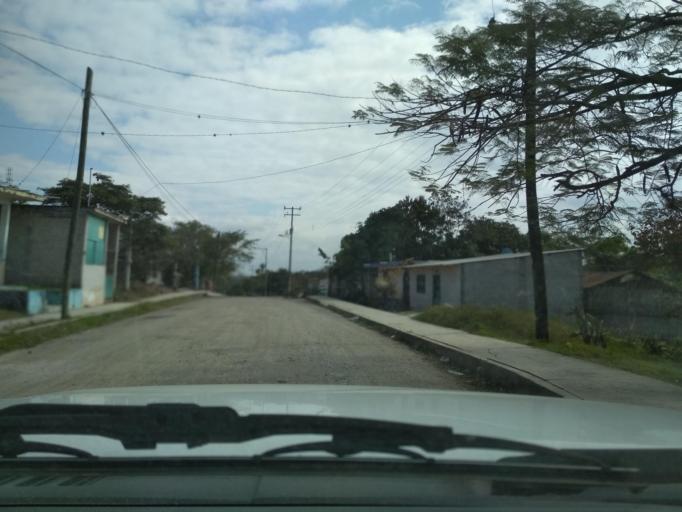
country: MX
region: Veracruz
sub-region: Coatepec
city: Tuzamapan
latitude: 19.3707
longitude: -96.8796
